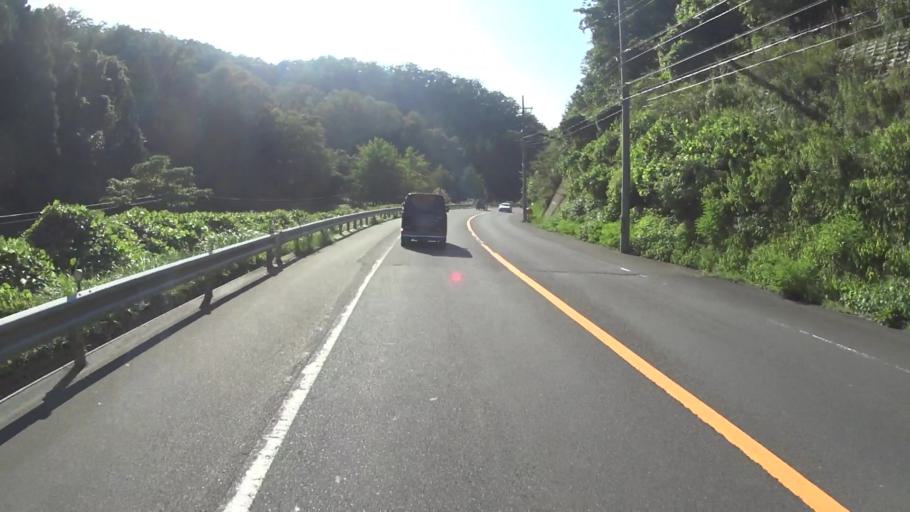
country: JP
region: Hyogo
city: Toyooka
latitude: 35.6588
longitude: 135.0022
